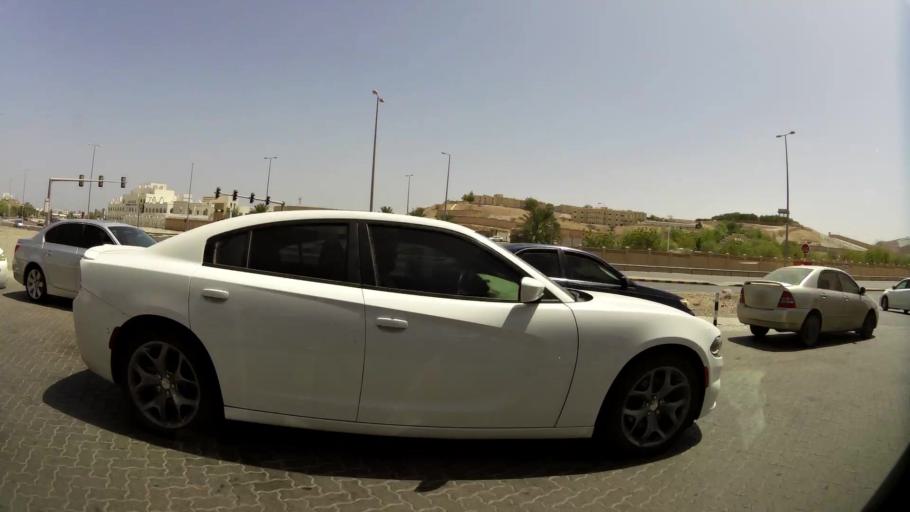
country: OM
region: Muhafazat Masqat
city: Bawshar
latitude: 23.5913
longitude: 58.4592
